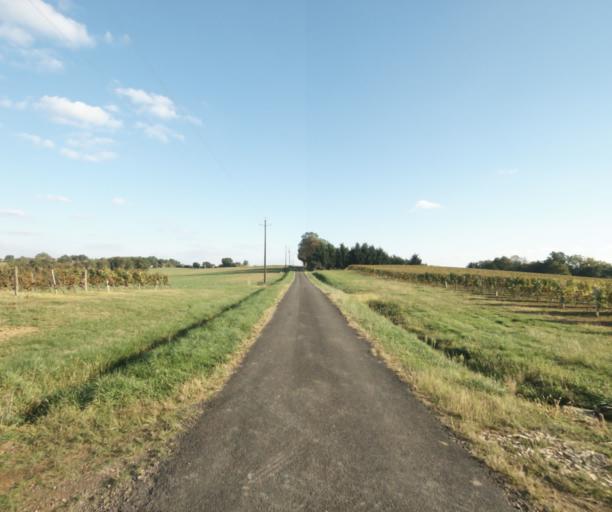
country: FR
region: Midi-Pyrenees
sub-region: Departement du Gers
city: Eauze
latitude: 43.7535
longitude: 0.1013
